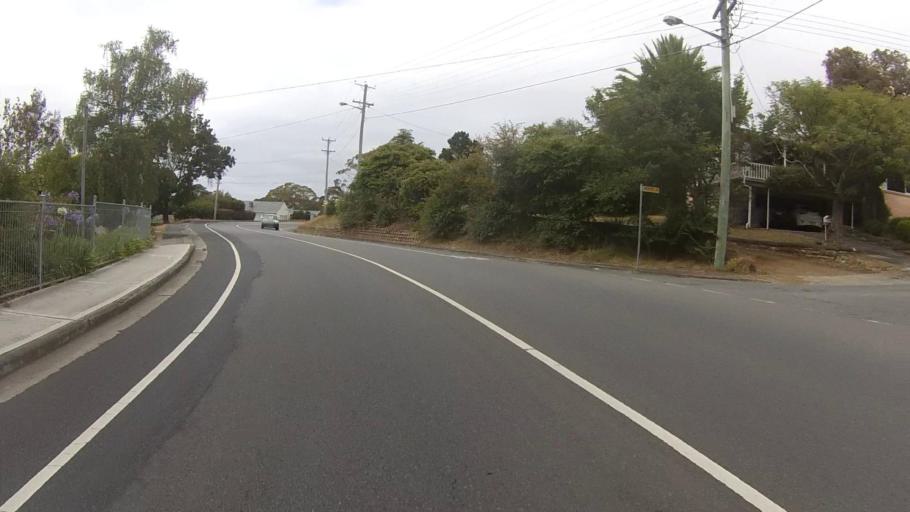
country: AU
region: Tasmania
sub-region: Kingborough
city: Taroona
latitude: -42.9352
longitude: 147.3541
